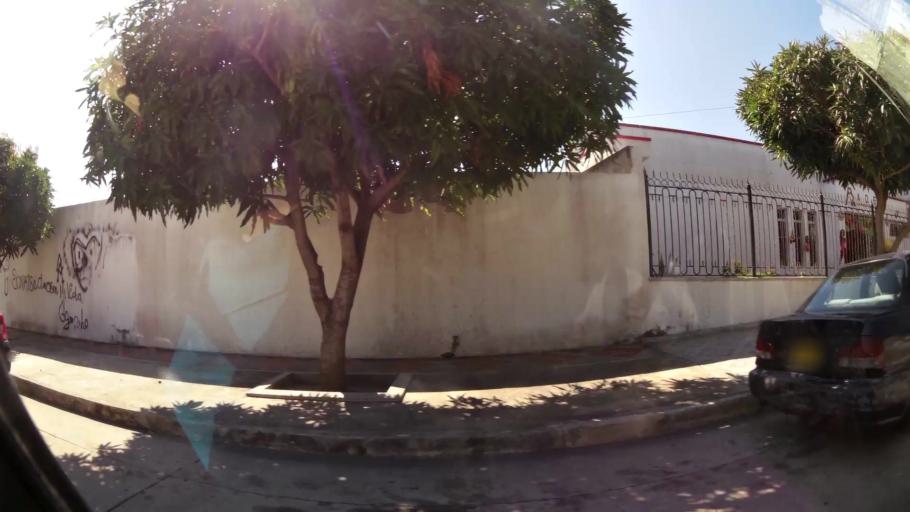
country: CO
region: Atlantico
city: Barranquilla
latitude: 10.9846
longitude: -74.8025
